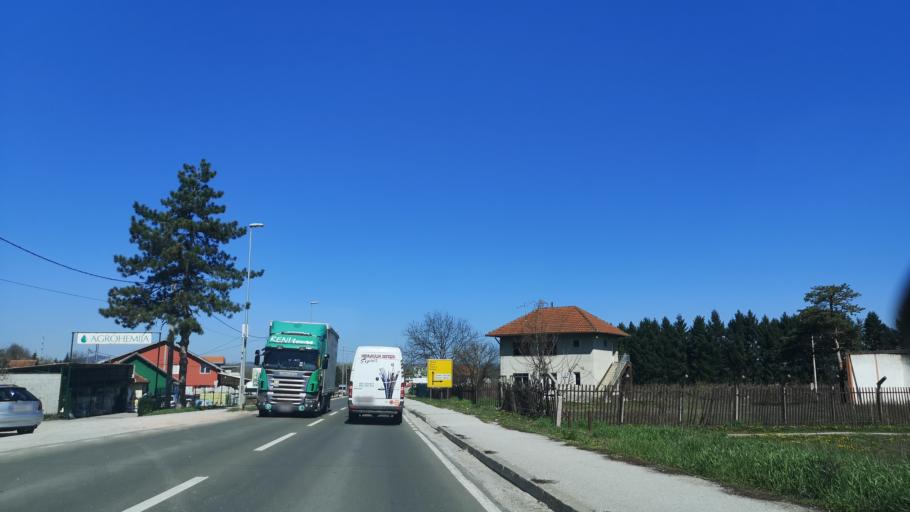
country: RS
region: Central Serbia
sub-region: Moravicki Okrug
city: Cacak
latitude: 43.8874
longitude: 20.3156
